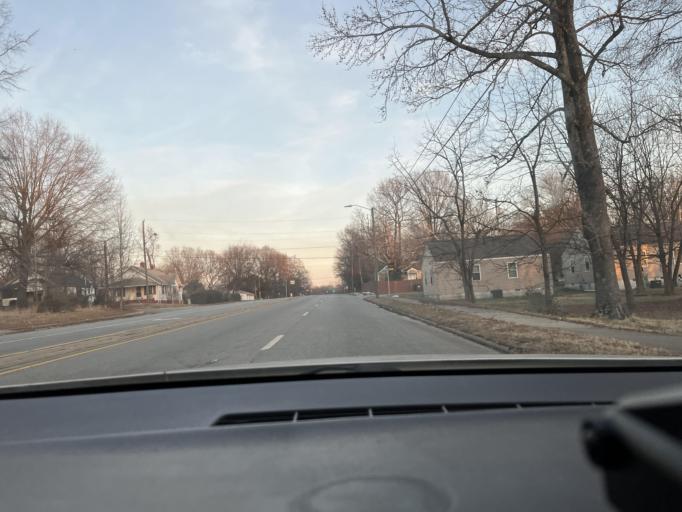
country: US
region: North Carolina
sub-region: Guilford County
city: Greensboro
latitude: 36.0629
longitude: -79.7647
